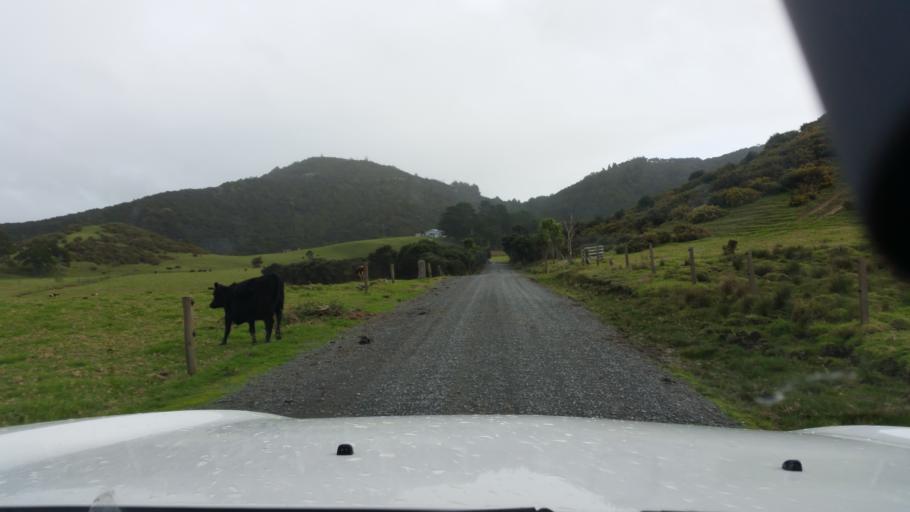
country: NZ
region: Northland
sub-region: Whangarei
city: Ruakaka
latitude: -35.7808
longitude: 174.5470
